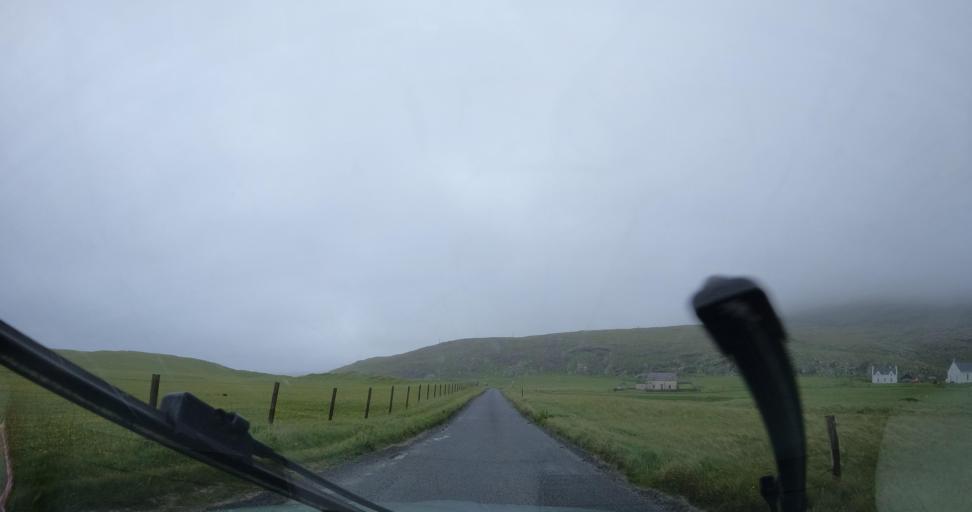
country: GB
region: Scotland
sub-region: Eilean Siar
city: Barra
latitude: 56.9857
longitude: -7.5090
